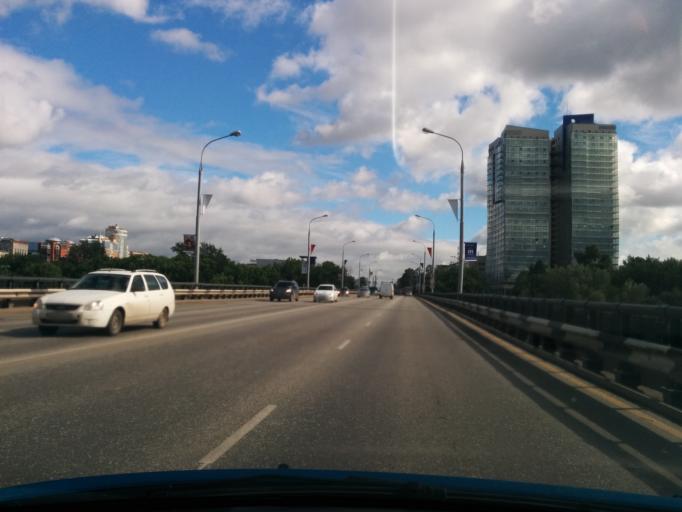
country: RU
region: Perm
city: Perm
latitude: 58.0173
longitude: 56.2223
